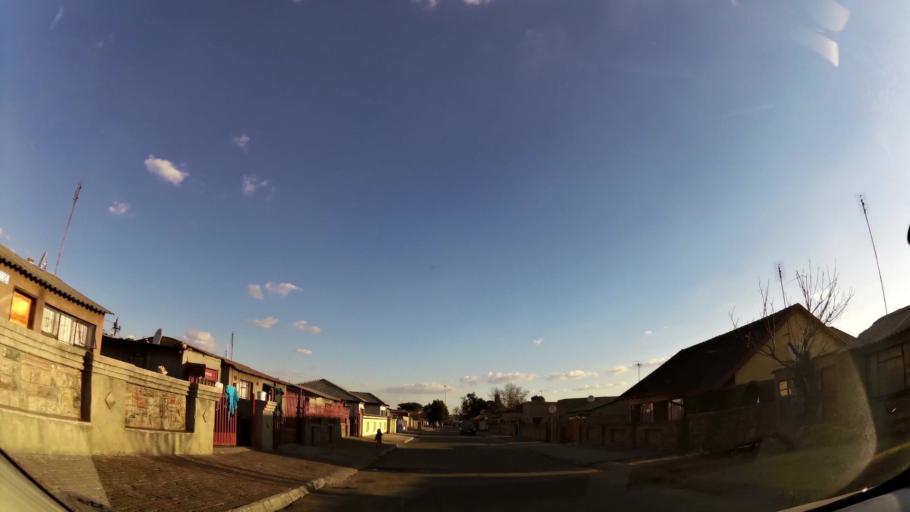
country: ZA
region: Mpumalanga
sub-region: Nkangala District Municipality
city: Witbank
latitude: -25.8806
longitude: 29.1877
